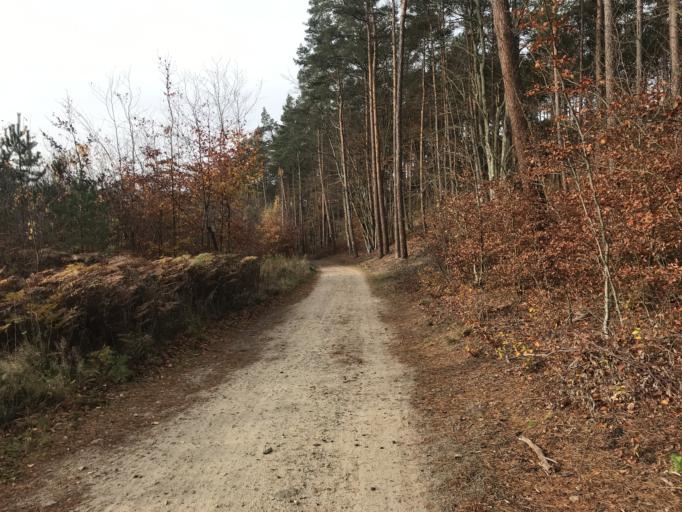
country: PL
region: Pomeranian Voivodeship
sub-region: Powiat pucki
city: Wierzchucino
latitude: 54.8292
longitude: 18.0296
